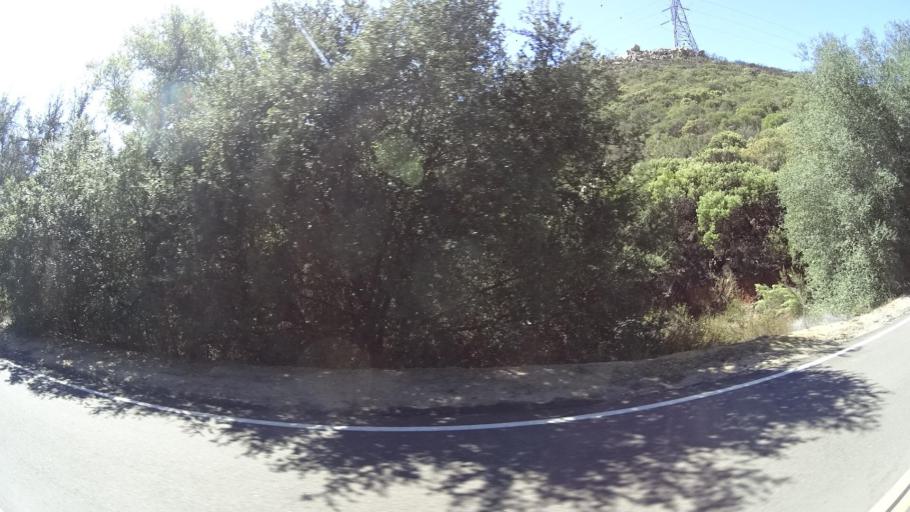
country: US
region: California
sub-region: San Diego County
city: Alpine
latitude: 32.7726
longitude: -116.7064
